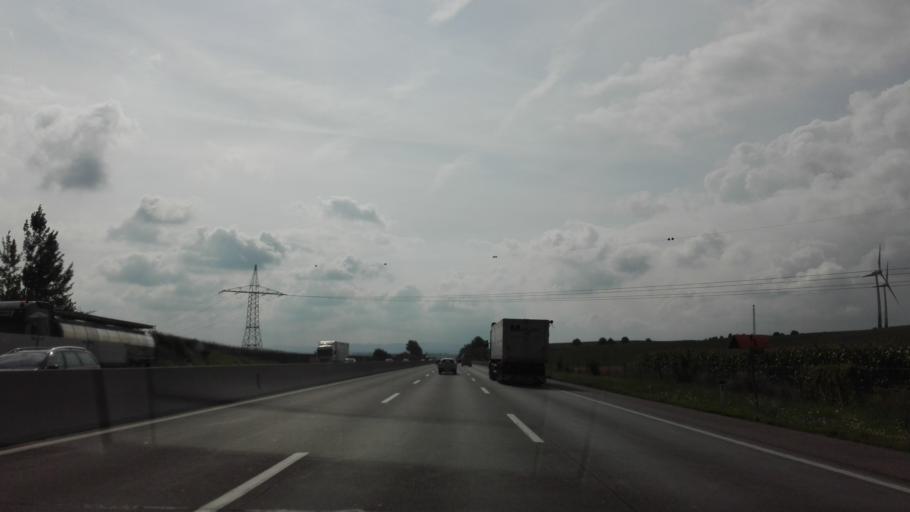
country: AT
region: Lower Austria
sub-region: Politischer Bezirk Sankt Polten
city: Haunoldstein
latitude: 48.1789
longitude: 15.4563
